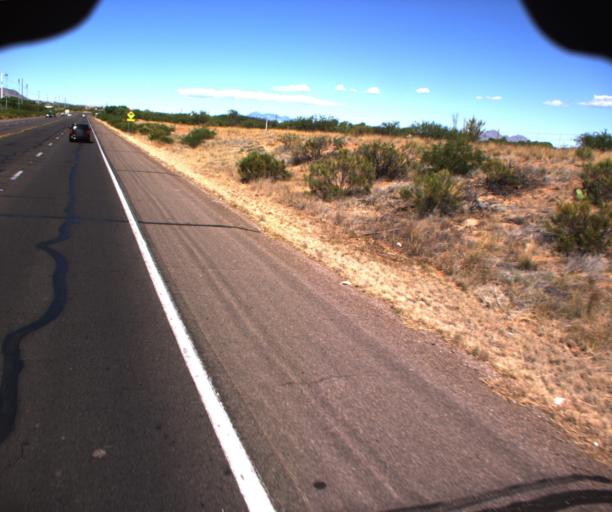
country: US
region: Arizona
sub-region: Cochise County
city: Sierra Vista
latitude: 31.5695
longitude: -110.2972
